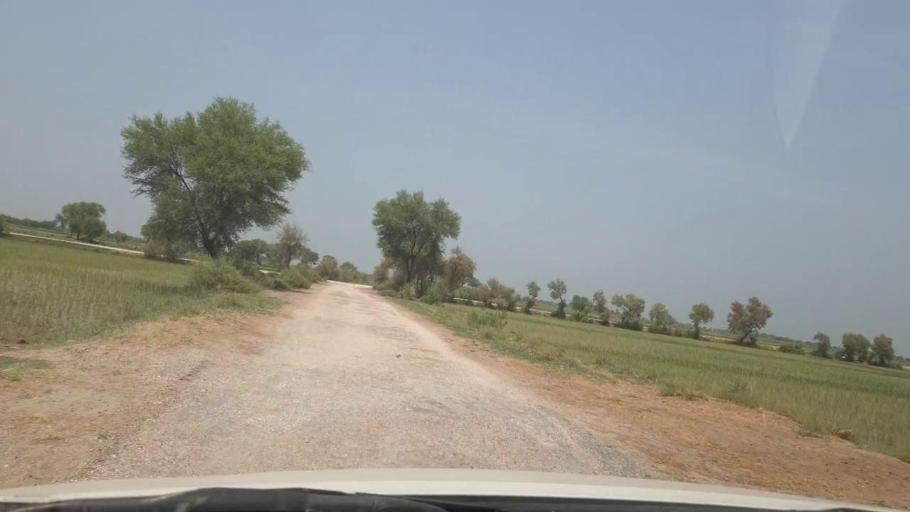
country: PK
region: Sindh
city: Rustam jo Goth
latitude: 28.0473
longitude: 68.7513
